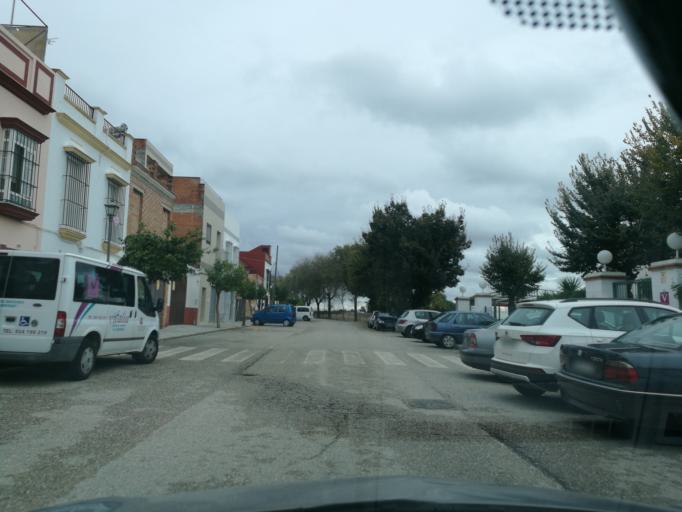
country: ES
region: Andalusia
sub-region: Provincia de Sevilla
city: La Campana
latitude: 37.5655
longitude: -5.4308
